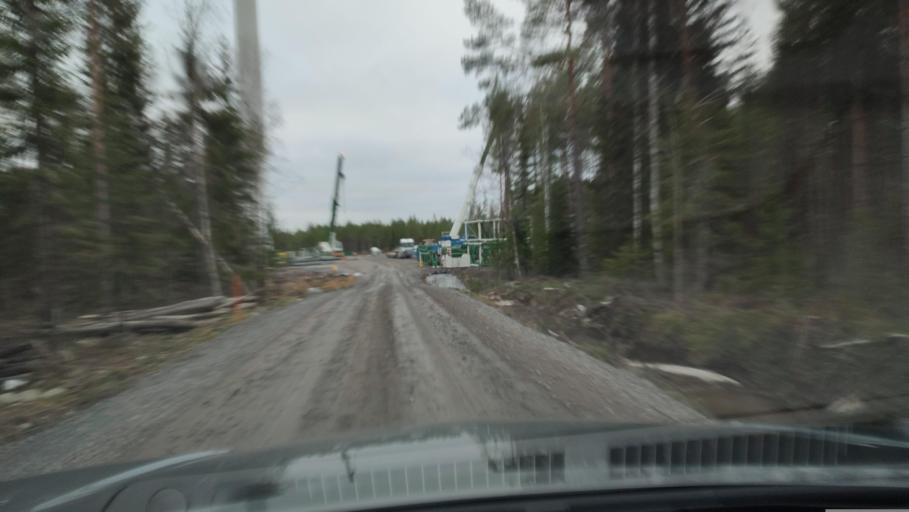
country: FI
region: Southern Ostrobothnia
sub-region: Suupohja
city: Karijoki
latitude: 62.2005
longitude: 21.5645
